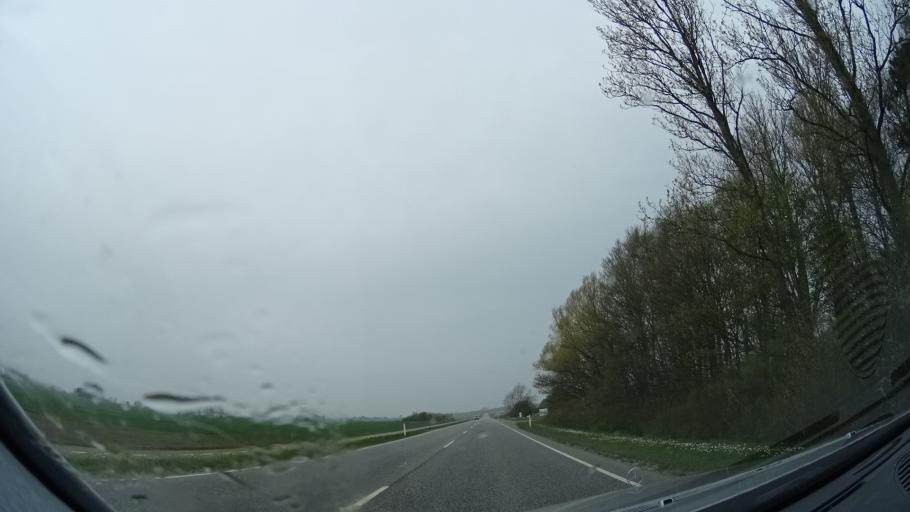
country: DK
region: Zealand
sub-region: Holbaek Kommune
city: Holbaek
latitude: 55.7347
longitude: 11.6323
